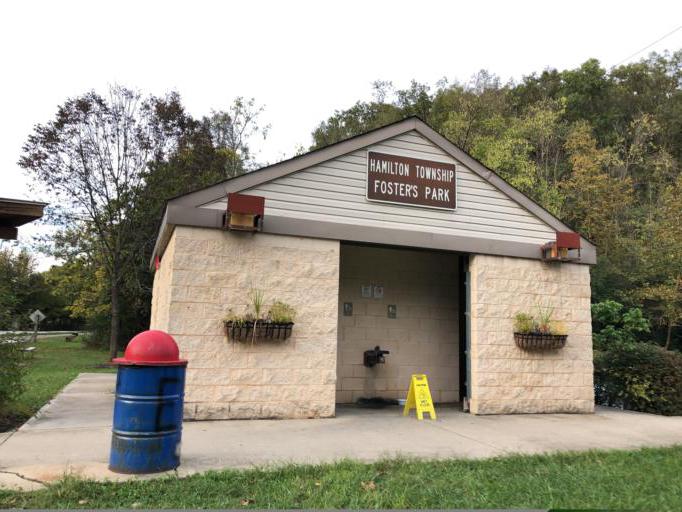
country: US
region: Ohio
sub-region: Warren County
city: Loveland Park
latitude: 39.3221
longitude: -84.2514
